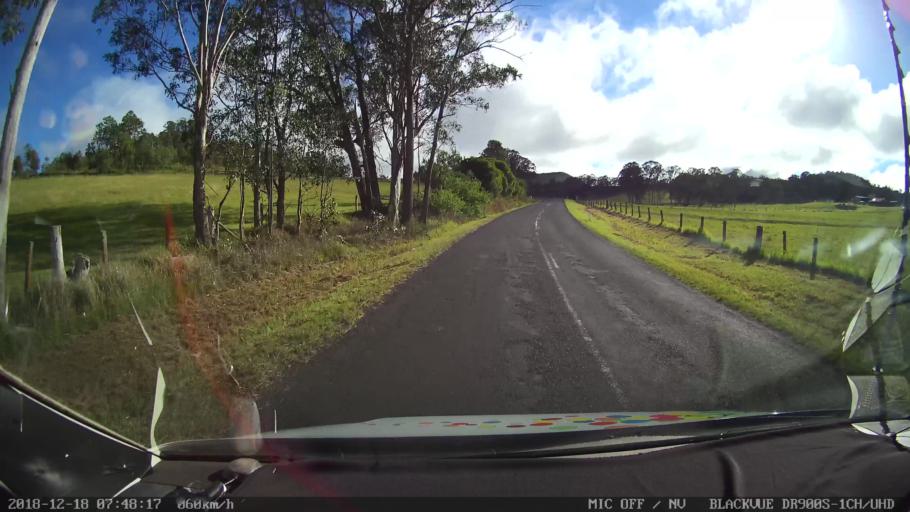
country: AU
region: New South Wales
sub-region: Kyogle
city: Kyogle
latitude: -28.4599
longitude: 152.5643
